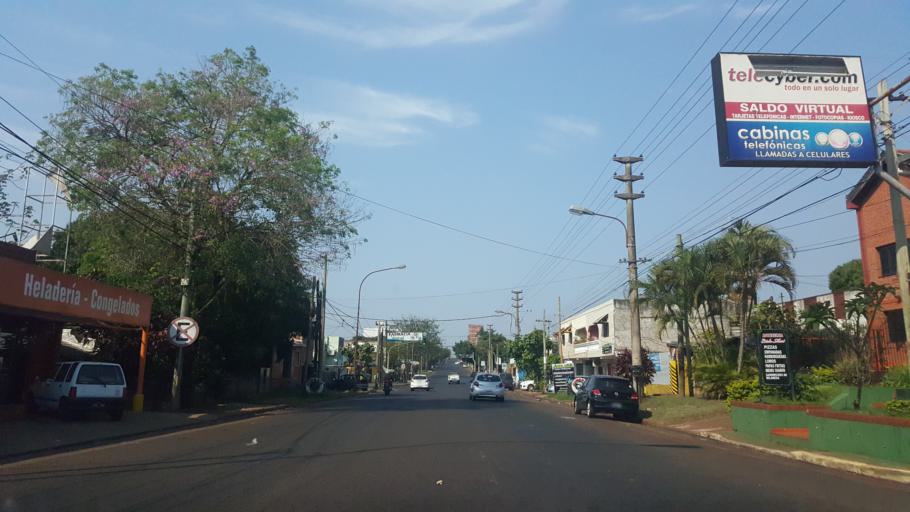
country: AR
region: Misiones
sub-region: Departamento de Capital
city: Posadas
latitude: -27.3829
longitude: -55.9036
